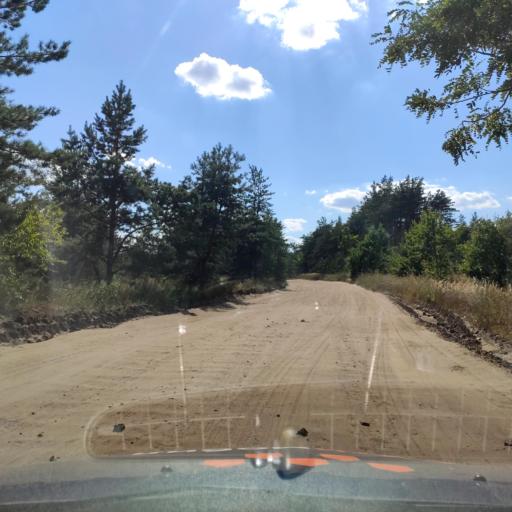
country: RU
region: Voronezj
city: Somovo
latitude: 51.7177
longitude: 39.3812
